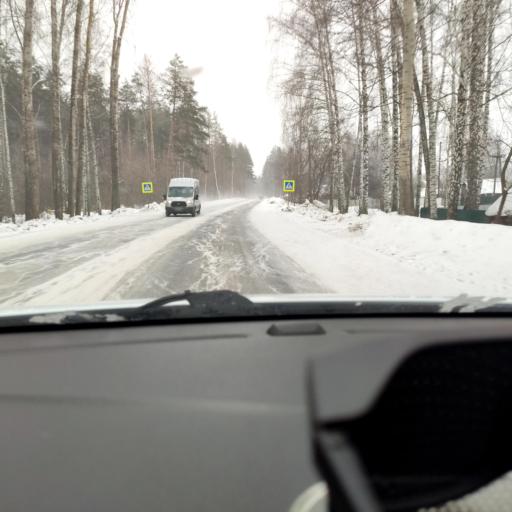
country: RU
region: Tatarstan
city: Vysokaya Gora
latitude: 55.9011
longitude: 49.2637
